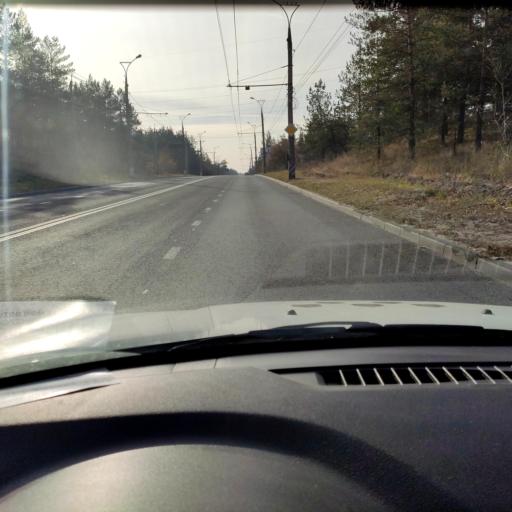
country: RU
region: Samara
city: Zhigulevsk
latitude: 53.5059
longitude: 49.4636
